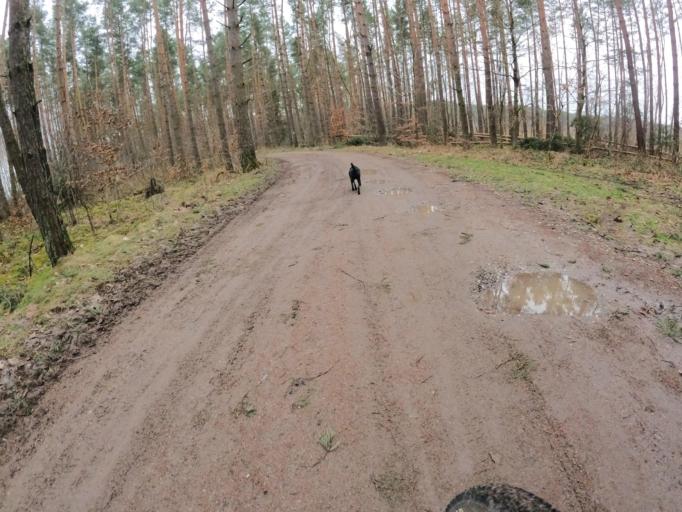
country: PL
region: West Pomeranian Voivodeship
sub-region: Powiat slawienski
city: Slawno
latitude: 54.2510
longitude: 16.6415
